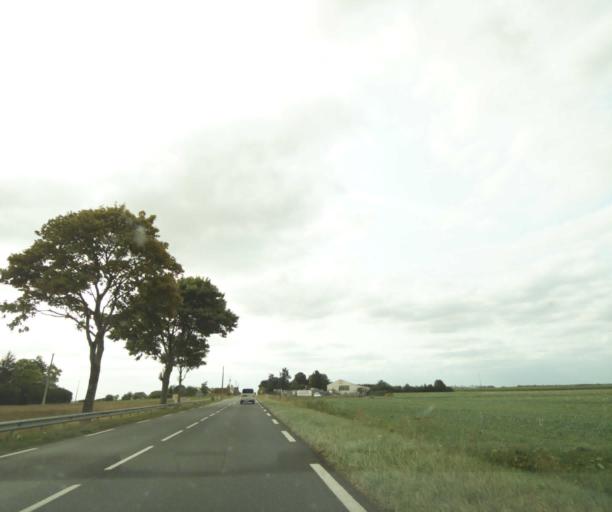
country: FR
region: Centre
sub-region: Departement d'Indre-et-Loire
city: Reignac-sur-Indre
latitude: 47.1950
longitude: 0.9222
